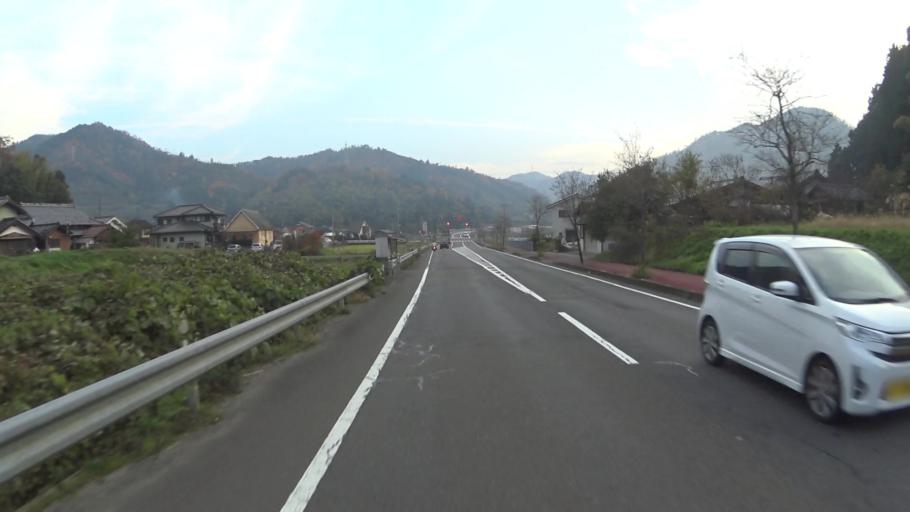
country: JP
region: Kyoto
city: Maizuru
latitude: 35.4662
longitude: 135.4232
